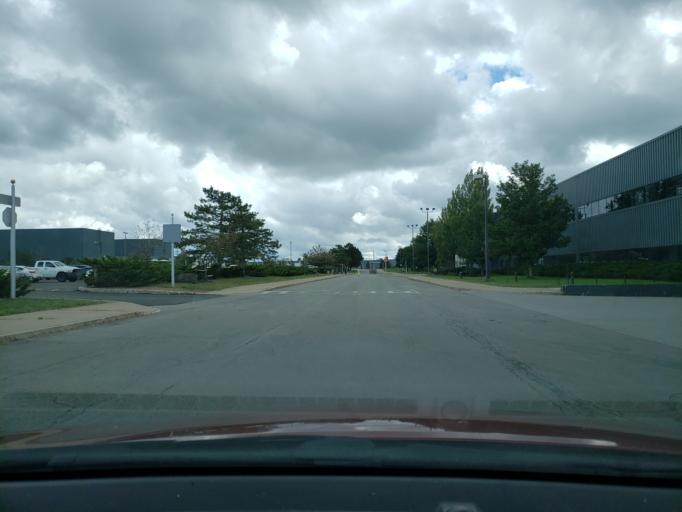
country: US
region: New York
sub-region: Monroe County
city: North Gates
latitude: 43.1536
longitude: -77.7441
